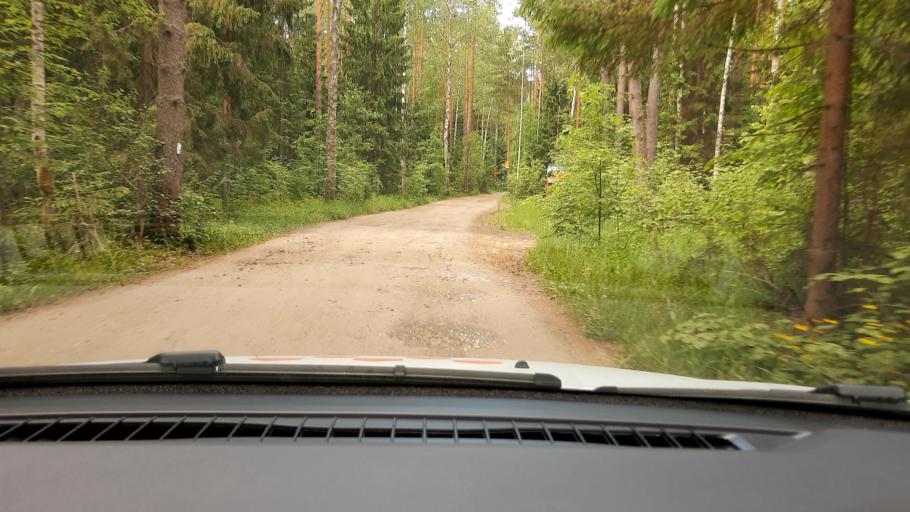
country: RU
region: Nizjnij Novgorod
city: Linda
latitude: 56.6760
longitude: 44.1801
